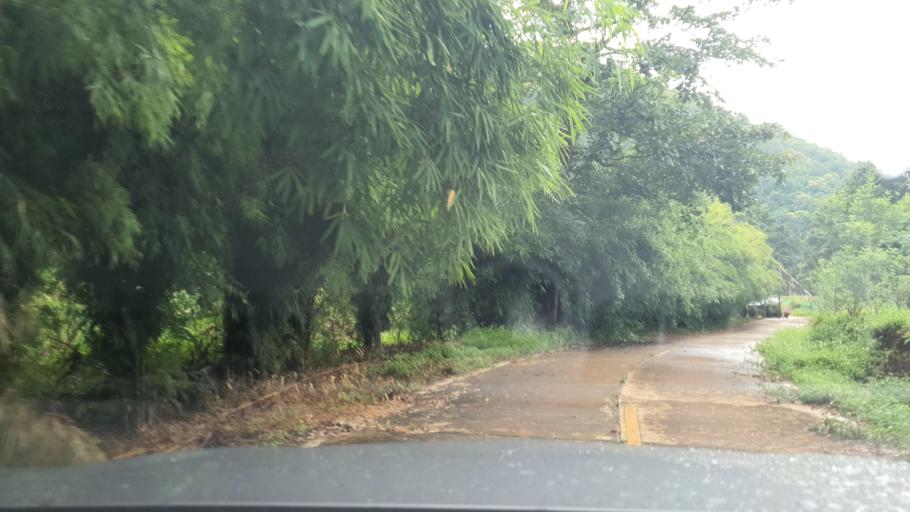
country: TH
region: Chiang Mai
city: Samoeng
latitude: 18.8334
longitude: 98.7754
